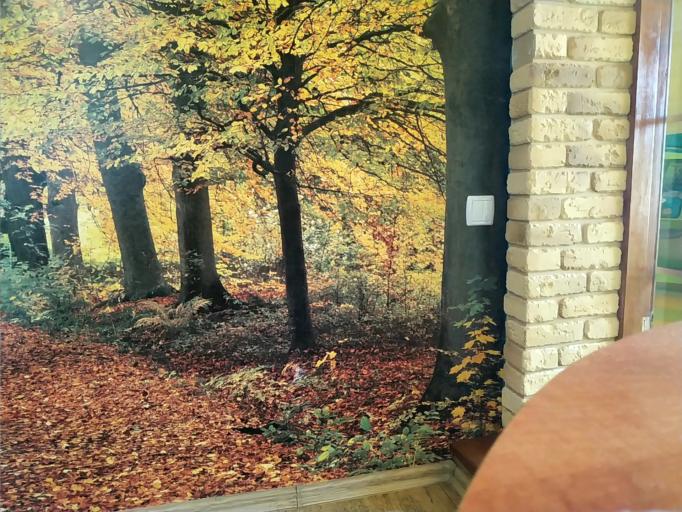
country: RU
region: Arkhangelskaya
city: Onega
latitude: 63.6932
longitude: 38.0911
